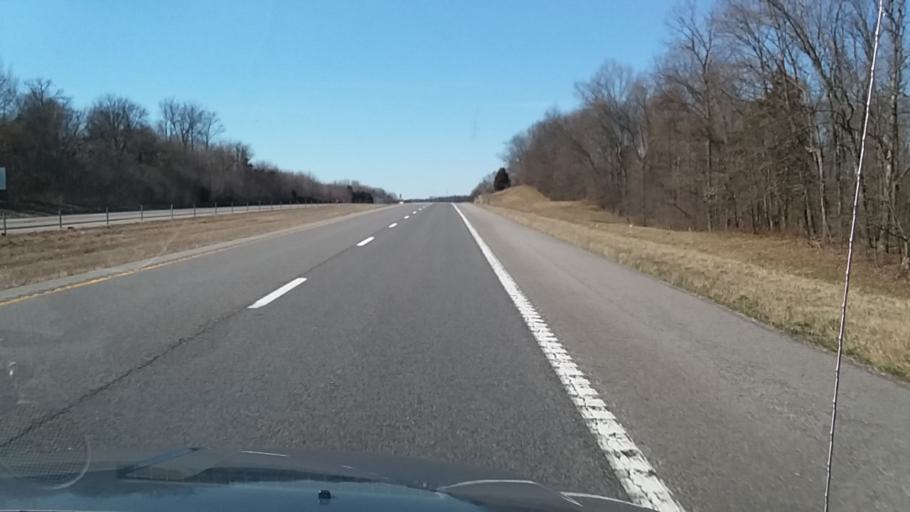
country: US
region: Missouri
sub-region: Perry County
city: Perryville
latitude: 37.5844
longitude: -89.7660
